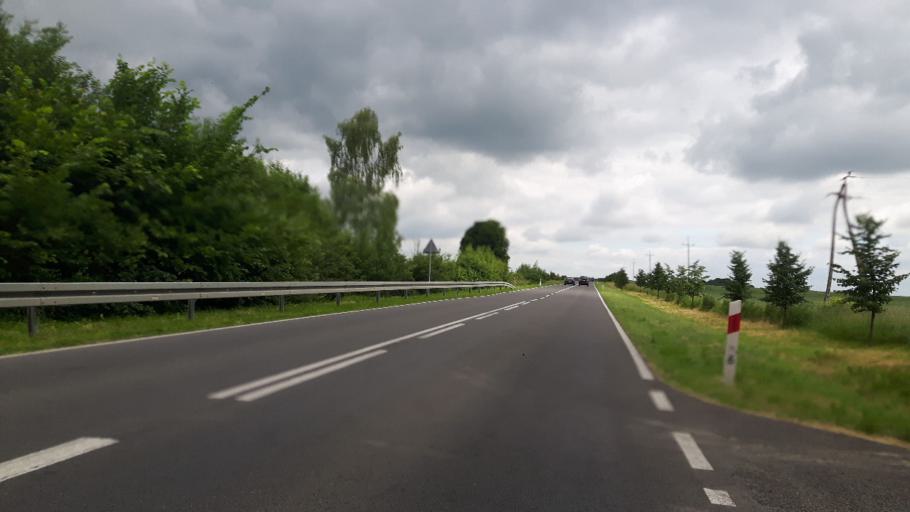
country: PL
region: West Pomeranian Voivodeship
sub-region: Powiat policki
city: Kolbaskowo
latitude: 53.3150
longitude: 14.4137
